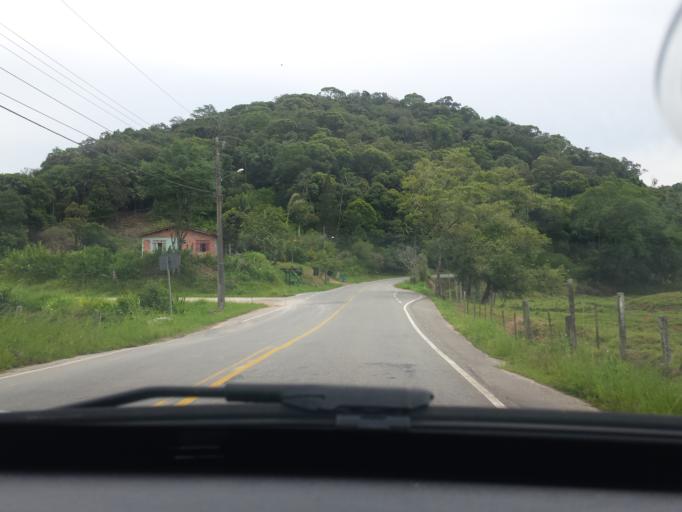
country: BR
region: Santa Catarina
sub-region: Blumenau
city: Blumenau
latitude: -26.8963
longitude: -49.0191
